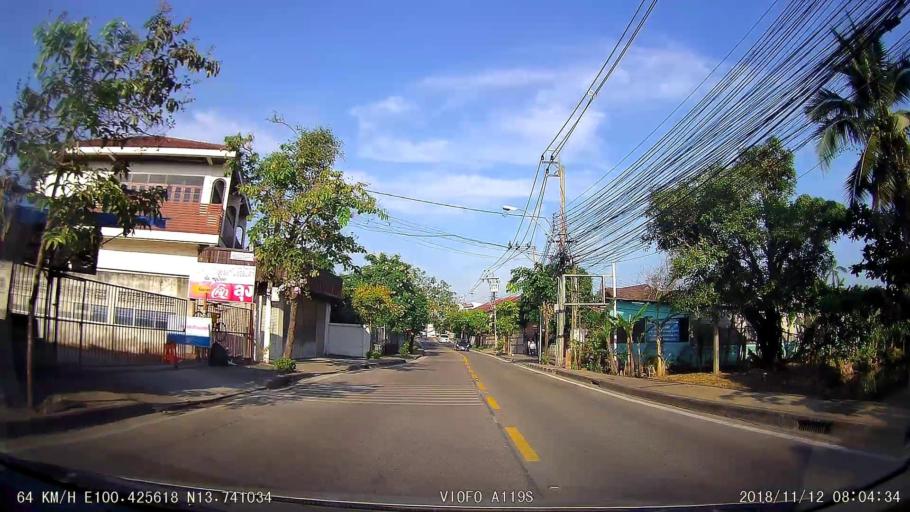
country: TH
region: Bangkok
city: Phasi Charoen
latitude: 13.7411
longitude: 100.4254
